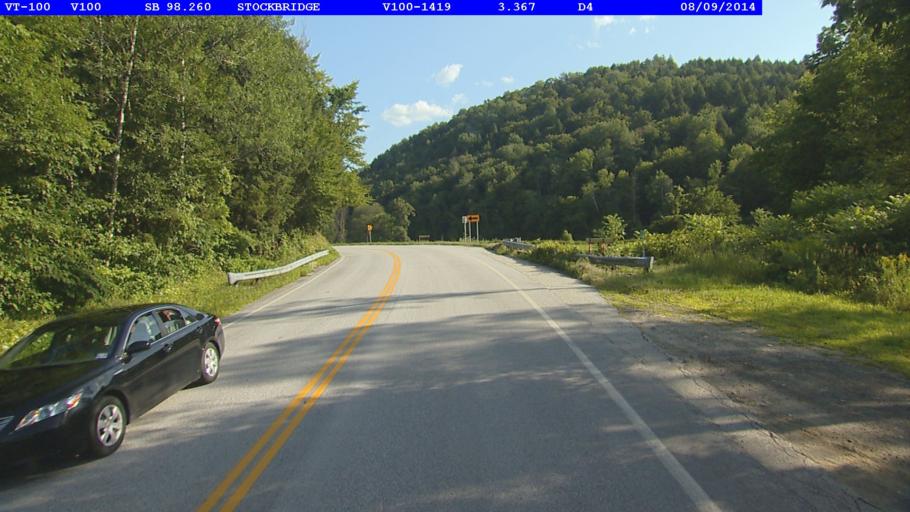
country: US
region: Vermont
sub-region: Orange County
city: Randolph
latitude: 43.7875
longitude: -72.7603
